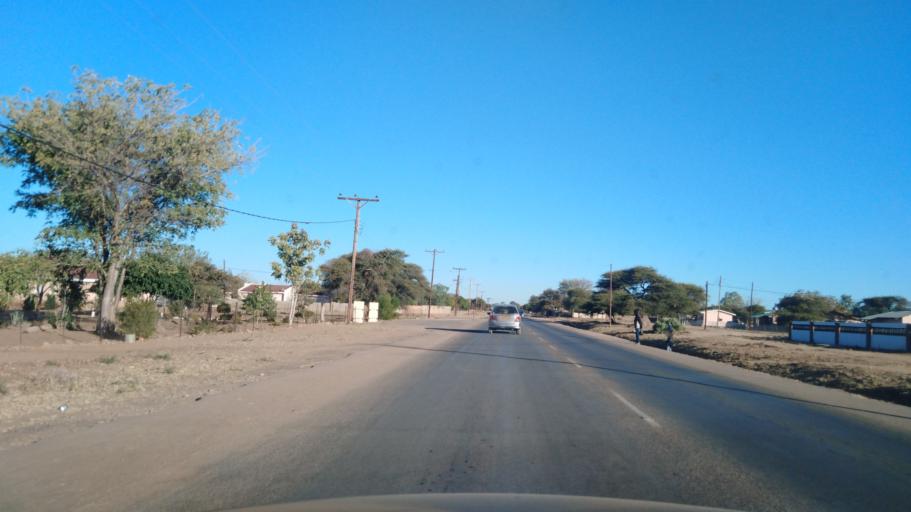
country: BW
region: Central
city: Mahalapye
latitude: -23.0937
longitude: 26.8264
